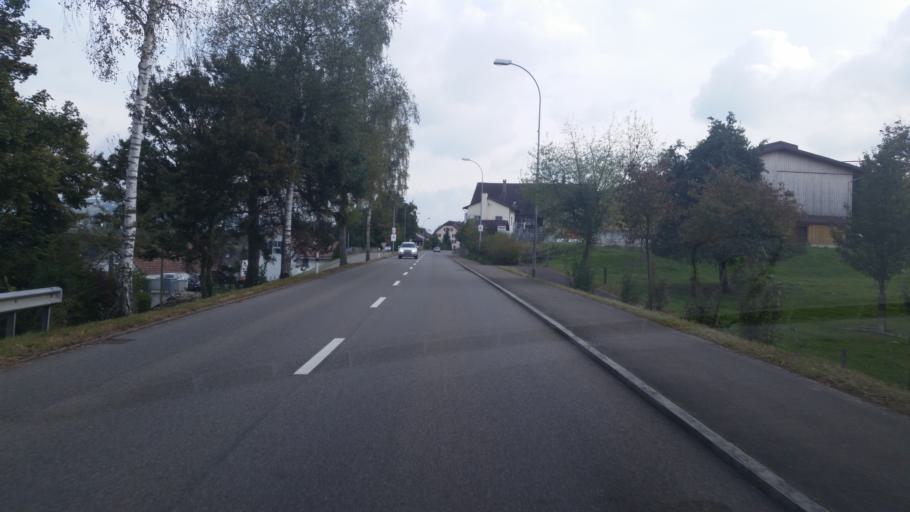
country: CH
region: Aargau
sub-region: Bezirk Baden
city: Kunten
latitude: 47.3694
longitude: 8.3101
